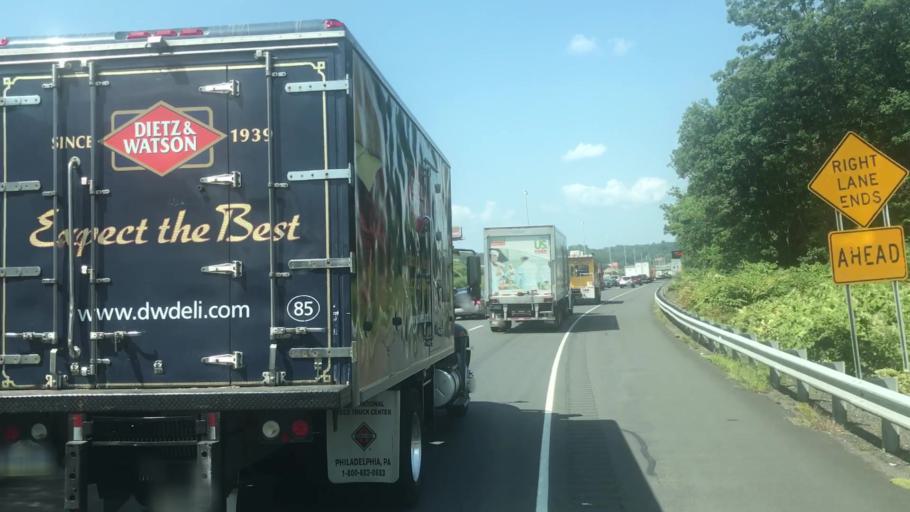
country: US
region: Connecticut
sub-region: New Haven County
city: Prospect
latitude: 41.5368
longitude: -72.9687
